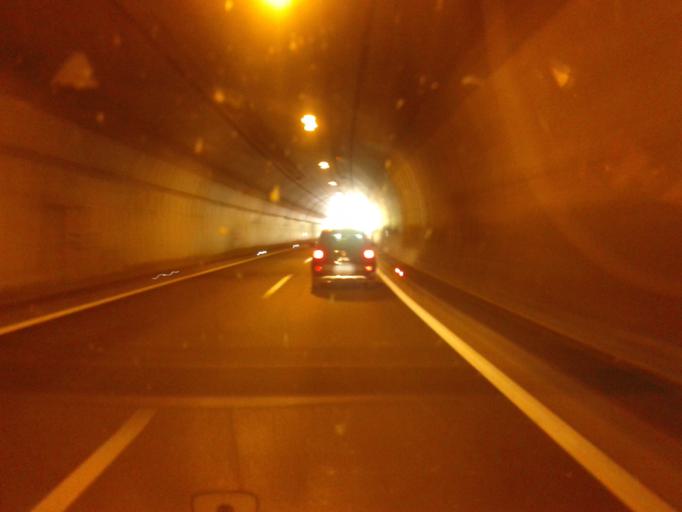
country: AT
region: Carinthia
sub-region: Politischer Bezirk Klagenfurt Land
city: Poggersdorf
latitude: 46.6412
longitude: 14.4314
